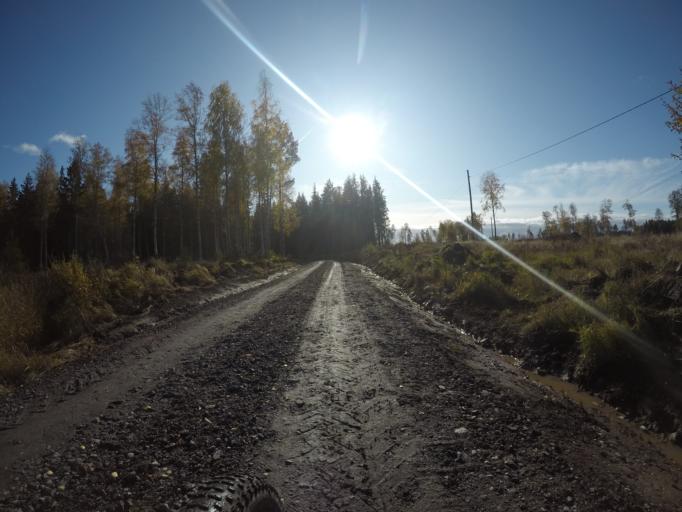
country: SE
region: Vaestmanland
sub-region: Kungsors Kommun
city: Kungsoer
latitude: 59.3113
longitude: 16.0978
